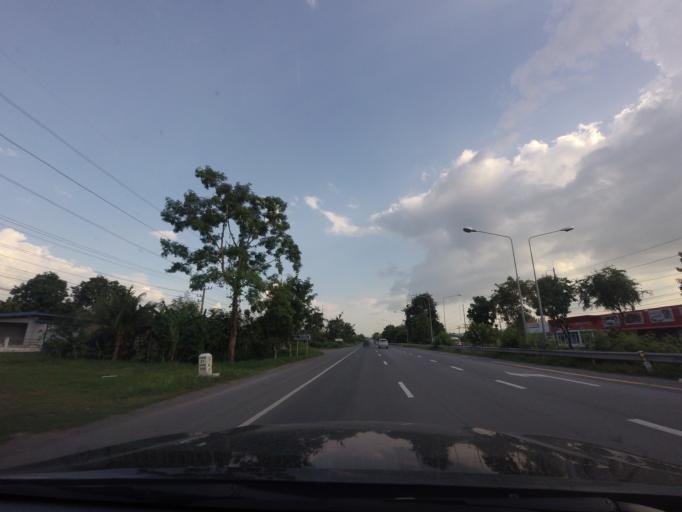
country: TH
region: Sara Buri
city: Saraburi
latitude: 14.5305
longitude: 100.8867
